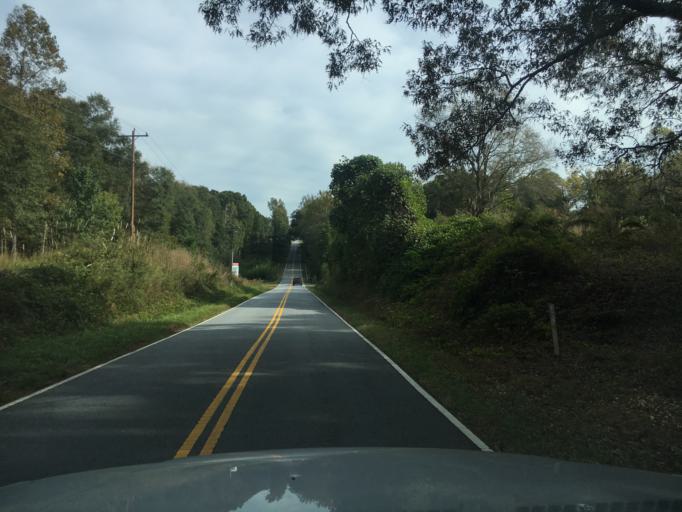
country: US
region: South Carolina
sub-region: Spartanburg County
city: Duncan
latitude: 34.9171
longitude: -82.1409
